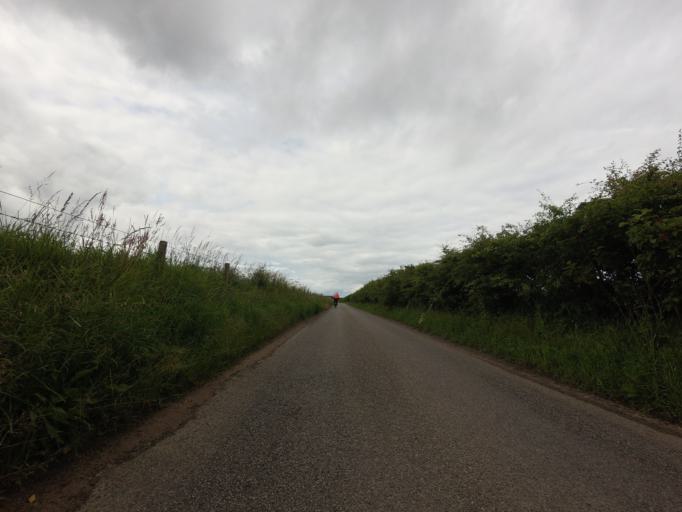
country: GB
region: Scotland
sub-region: Moray
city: Forres
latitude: 57.6221
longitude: -3.6676
